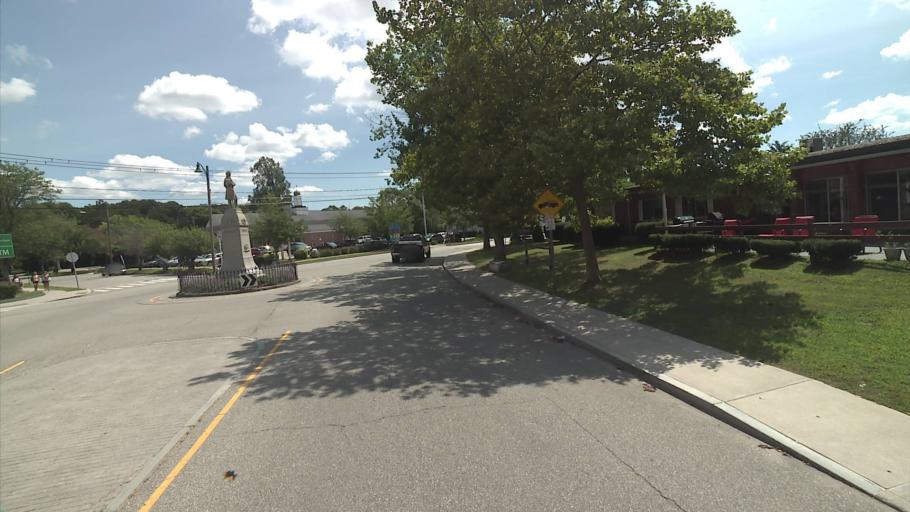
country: US
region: Connecticut
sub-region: New London County
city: Mystic
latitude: 41.3530
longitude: -71.9643
